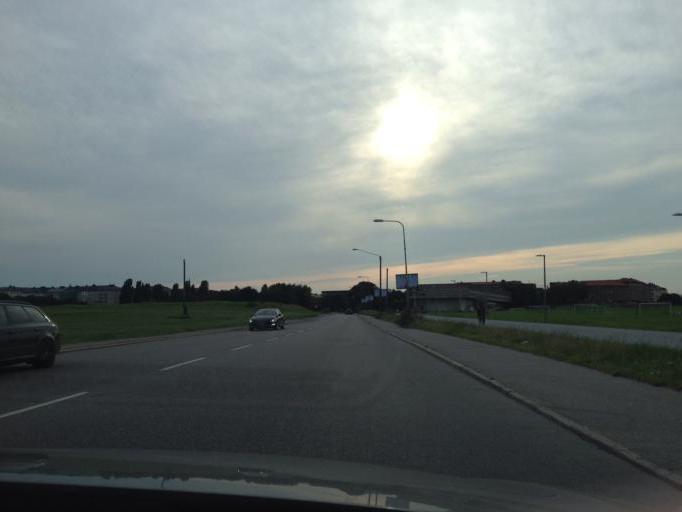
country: SE
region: Stockholm
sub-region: Stockholms Kommun
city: OEstermalm
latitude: 59.3395
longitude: 18.1116
